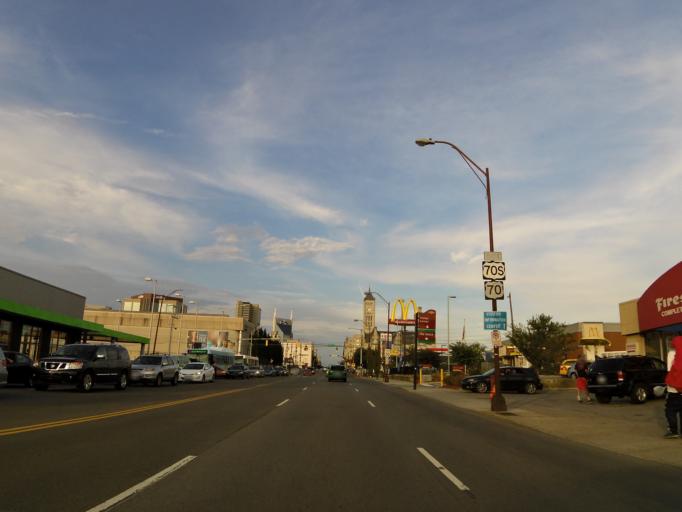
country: US
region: Tennessee
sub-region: Davidson County
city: Nashville
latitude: 36.1561
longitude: -86.7885
